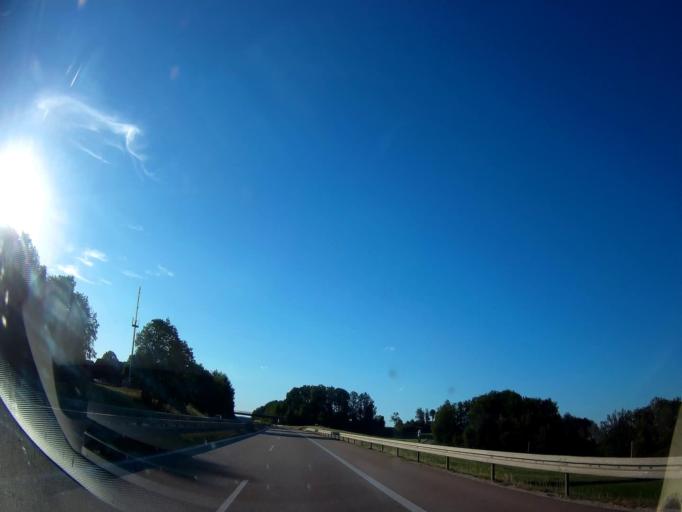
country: DE
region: Bavaria
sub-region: Upper Palatinate
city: Brunn
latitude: 49.1302
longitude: 11.8692
